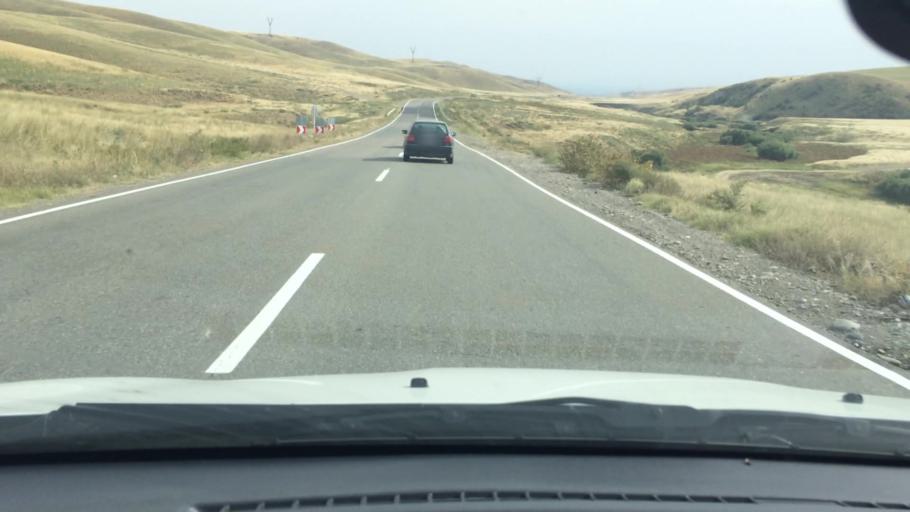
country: GE
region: Kvemo Kartli
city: Rust'avi
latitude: 41.5212
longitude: 44.9387
